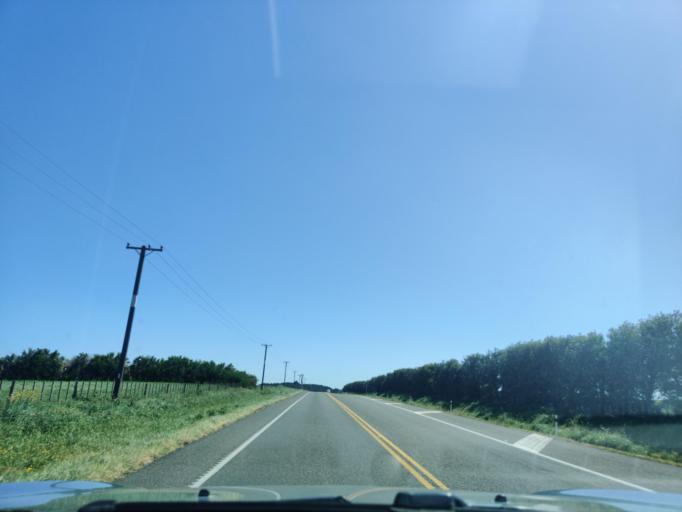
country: NZ
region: Taranaki
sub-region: South Taranaki District
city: Patea
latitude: -39.6965
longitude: 174.4308
